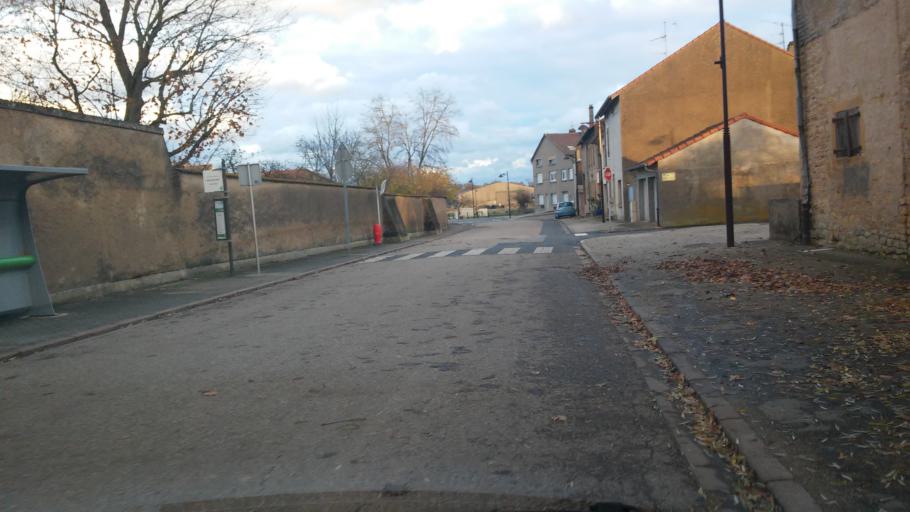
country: FR
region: Lorraine
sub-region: Departement de la Moselle
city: Argancy
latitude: 49.2196
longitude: 6.1935
